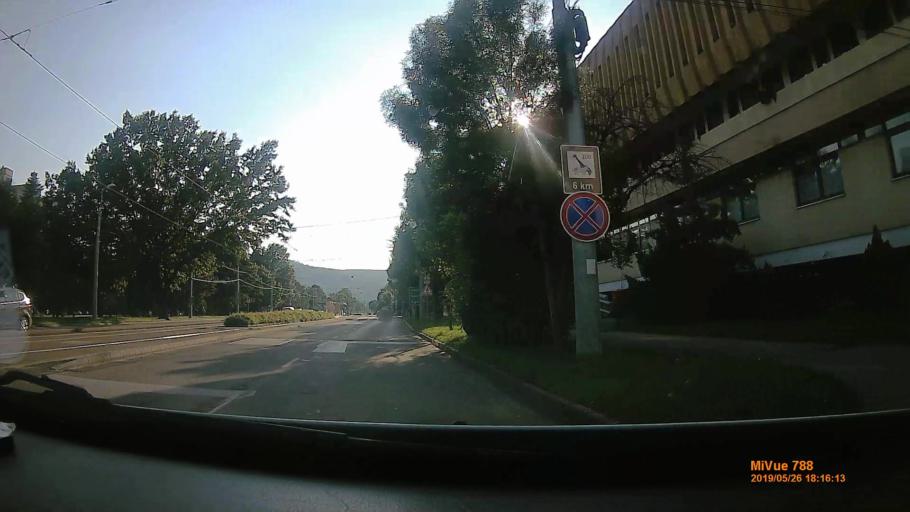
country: HU
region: Borsod-Abauj-Zemplen
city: Sajobabony
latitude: 48.1003
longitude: 20.7103
